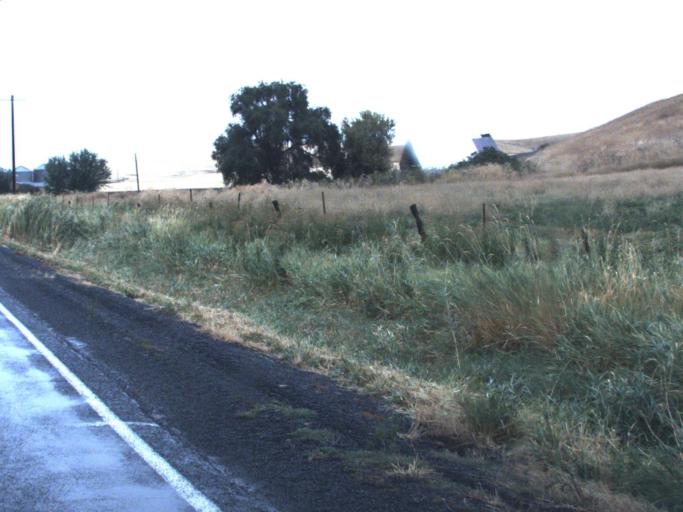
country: US
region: Washington
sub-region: Whitman County
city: Colfax
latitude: 47.0466
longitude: -117.5155
